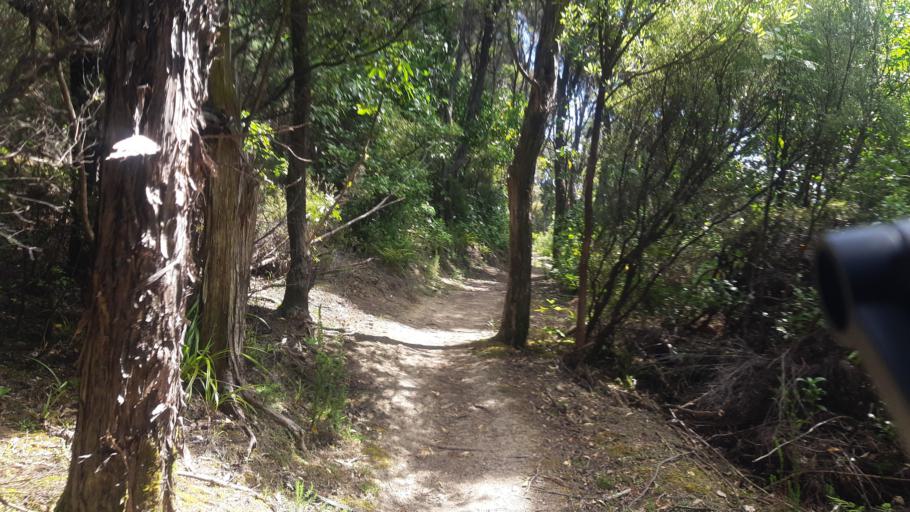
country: NZ
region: Marlborough
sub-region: Marlborough District
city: Picton
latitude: -41.2522
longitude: 174.0452
